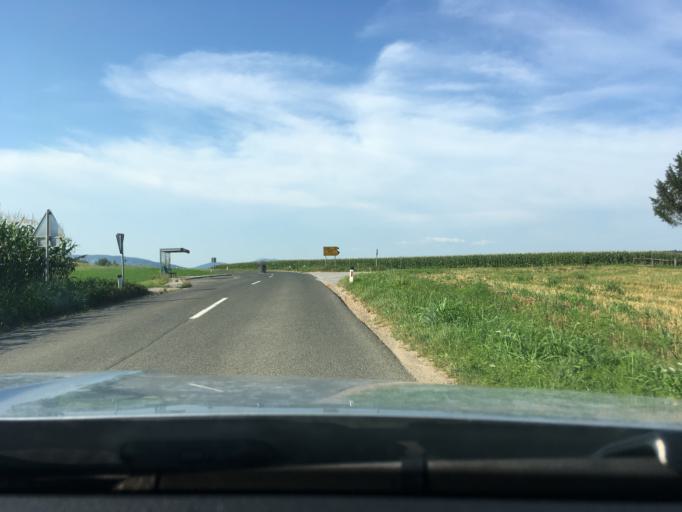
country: SI
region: Crnomelj
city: Crnomelj
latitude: 45.5296
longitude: 15.1631
